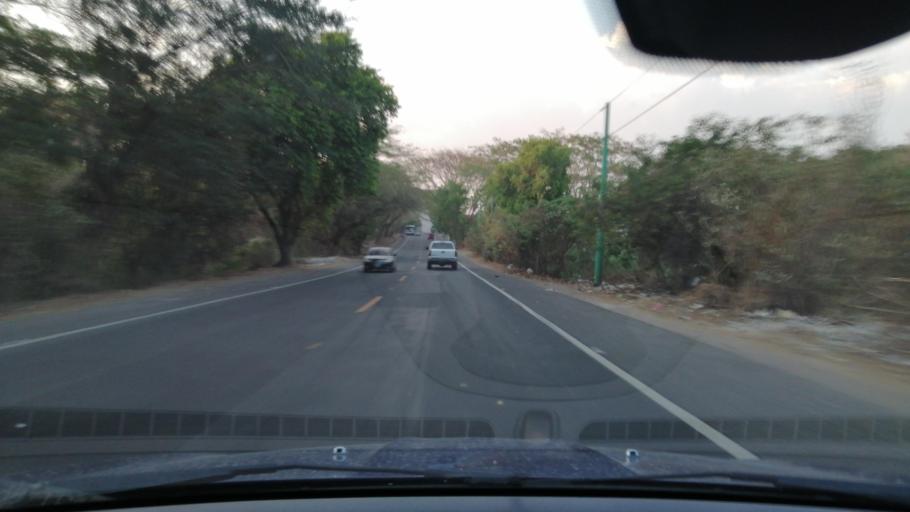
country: SV
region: Santa Ana
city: Santa Ana
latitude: 13.9976
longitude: -89.5414
